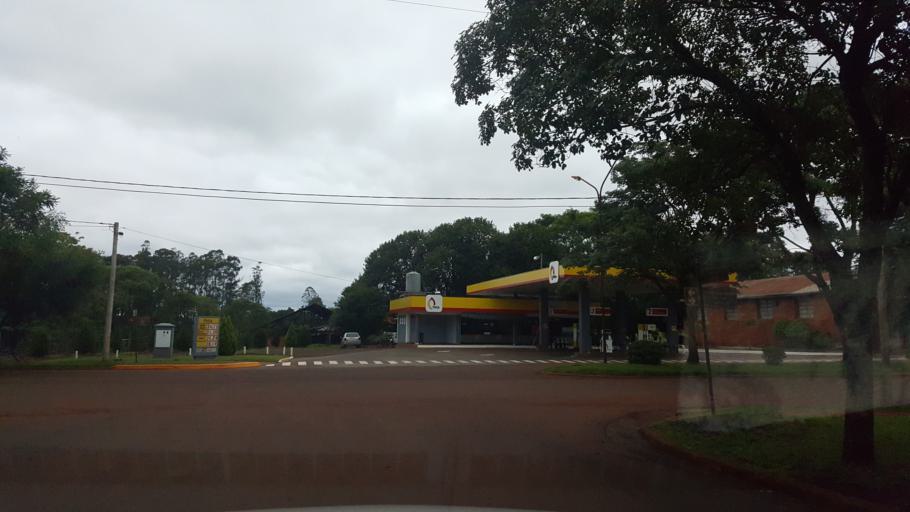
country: AR
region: Misiones
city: Ruiz de Montoya
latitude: -26.9684
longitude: -55.0574
